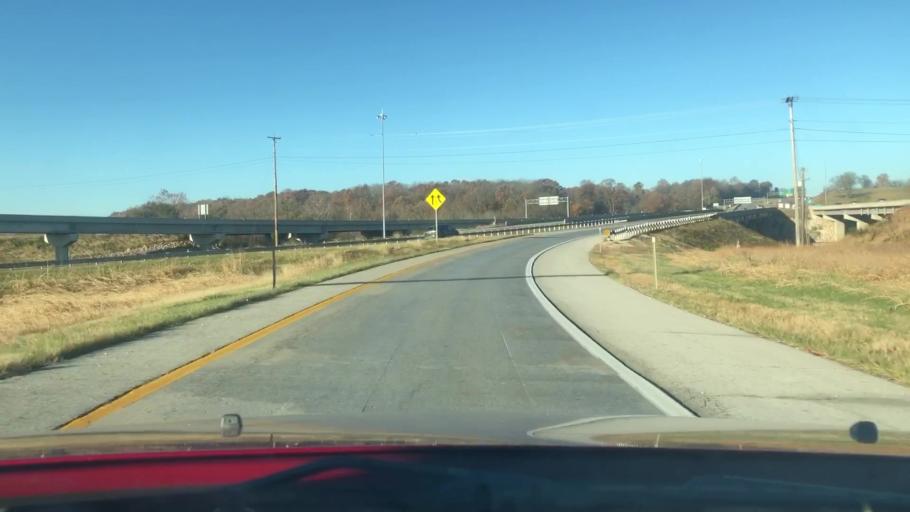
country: US
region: Missouri
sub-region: Christian County
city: Nixa
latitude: 37.1294
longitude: -93.2325
